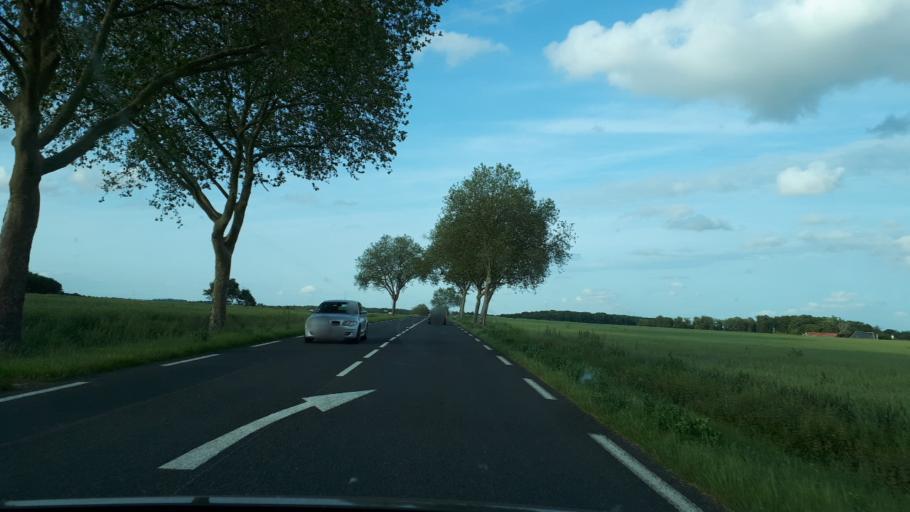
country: FR
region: Centre
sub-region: Departement d'Indre-et-Loire
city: Villedomer
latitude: 47.5380
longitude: 0.8491
